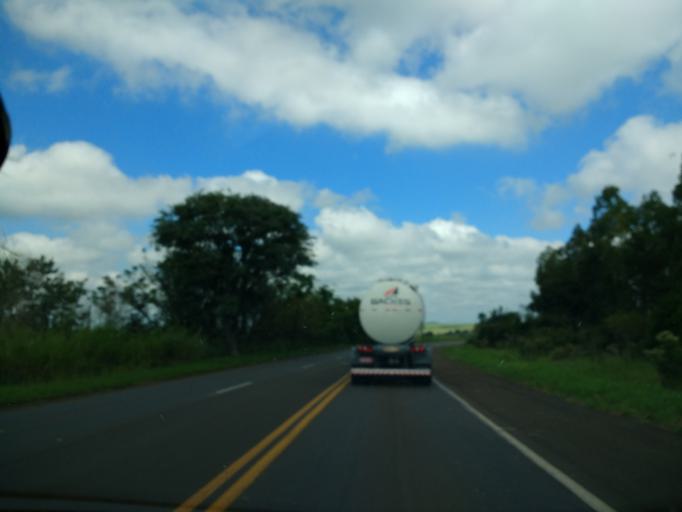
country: BR
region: Parana
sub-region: Cruzeiro Do Oeste
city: Cruzeiro do Oeste
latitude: -23.7850
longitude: -53.0262
